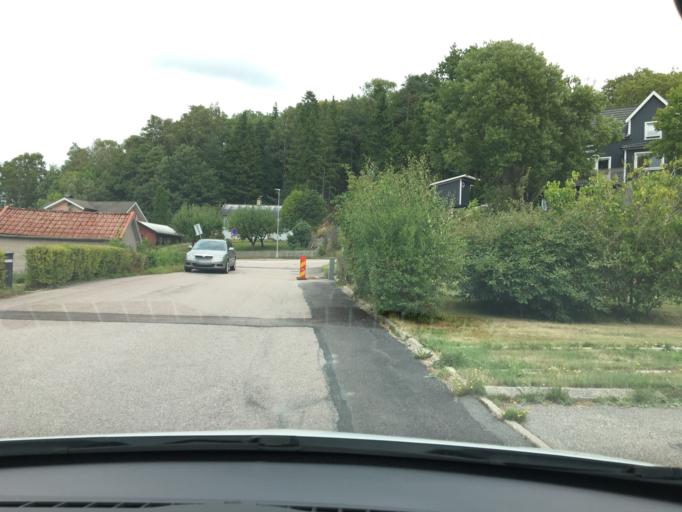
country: SE
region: Vaestra Goetaland
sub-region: Ale Kommun
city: Nodinge-Nol
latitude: 57.9115
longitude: 12.0574
